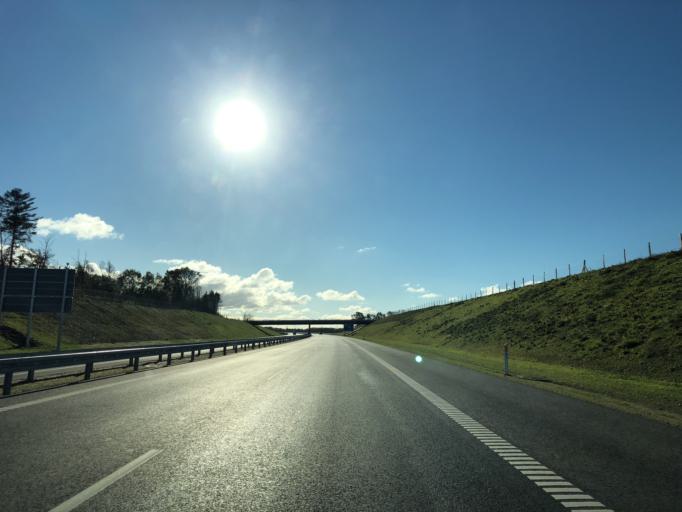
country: DK
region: Central Jutland
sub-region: Herning Kommune
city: Avlum
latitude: 56.3071
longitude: 8.7266
